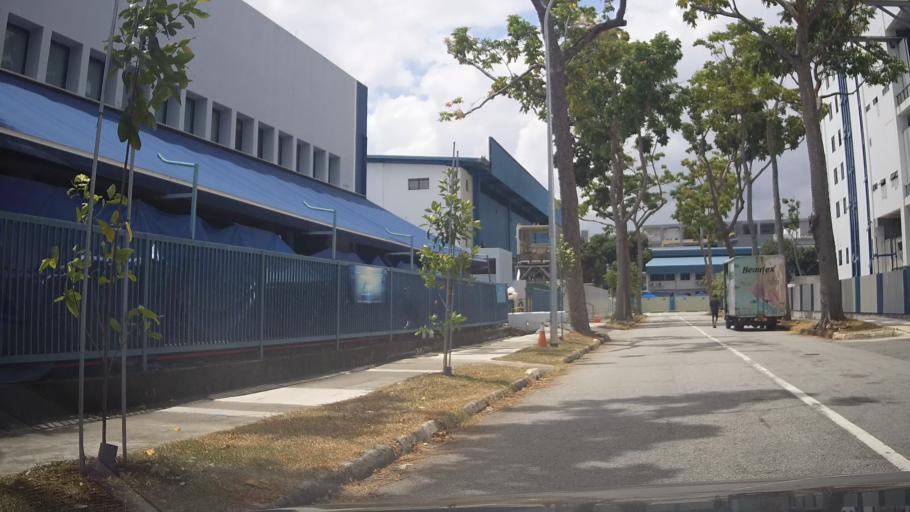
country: MY
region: Johor
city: Kampung Pasir Gudang Baru
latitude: 1.3834
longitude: 103.9728
